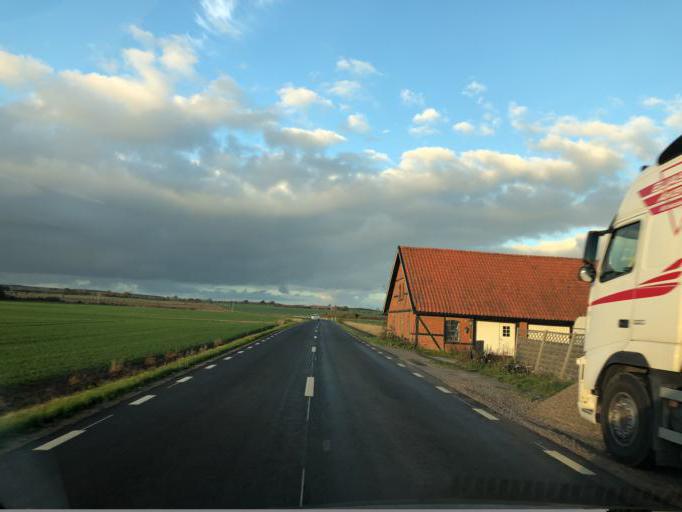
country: SE
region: Skane
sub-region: Svalovs Kommun
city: Svaloev
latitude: 55.9056
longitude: 13.1958
